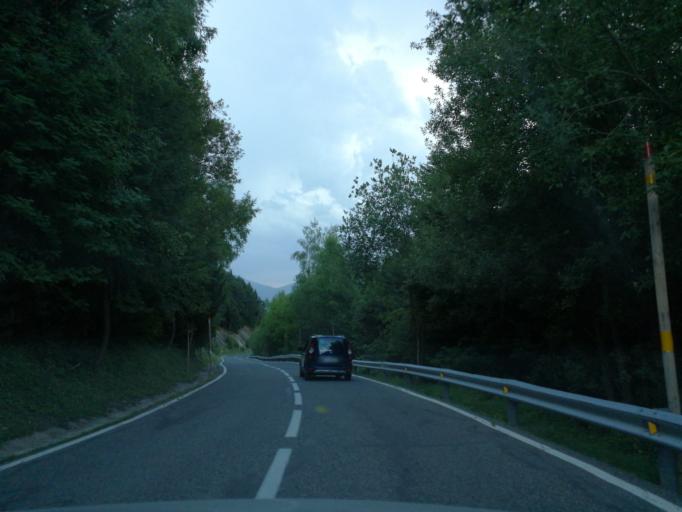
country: AD
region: Ordino
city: Ordino
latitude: 42.5552
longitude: 1.5523
